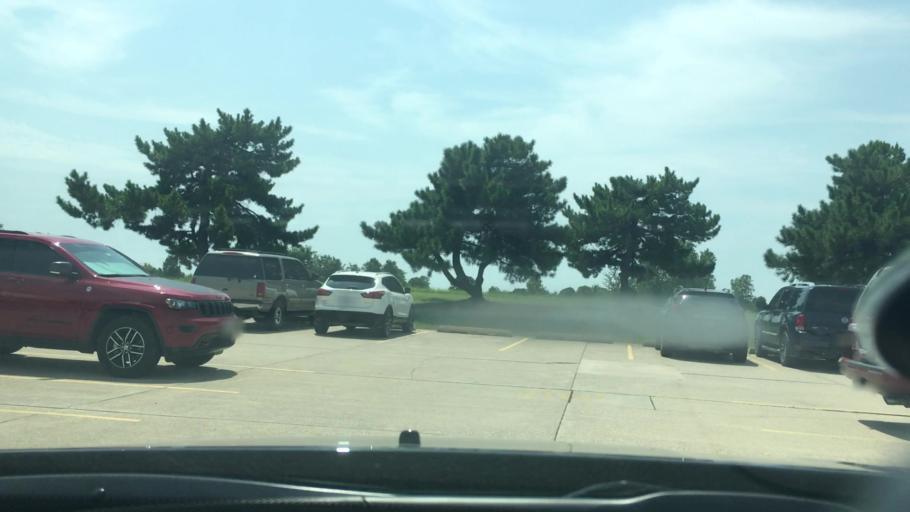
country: US
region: Oklahoma
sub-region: Pontotoc County
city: Ada
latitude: 34.7777
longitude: -96.6320
